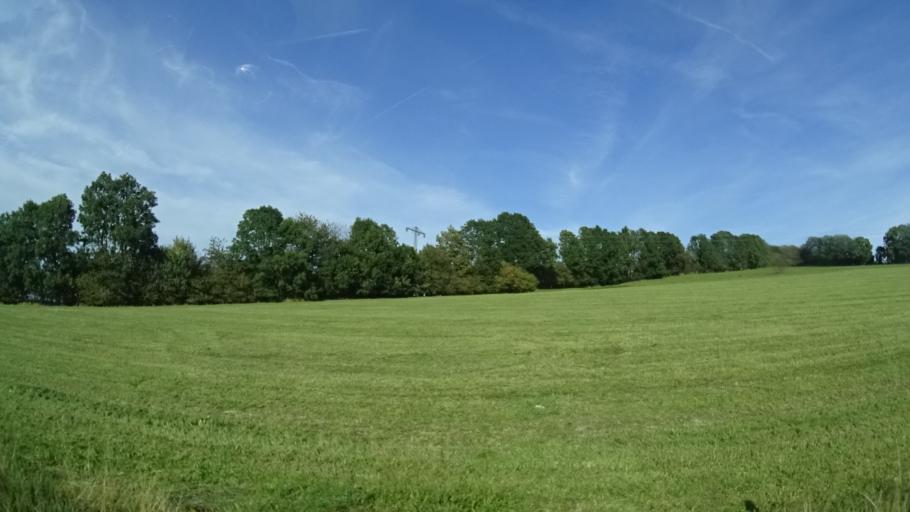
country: DE
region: Hesse
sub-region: Regierungsbezirk Kassel
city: Poppenhausen
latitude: 50.5276
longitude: 9.8657
